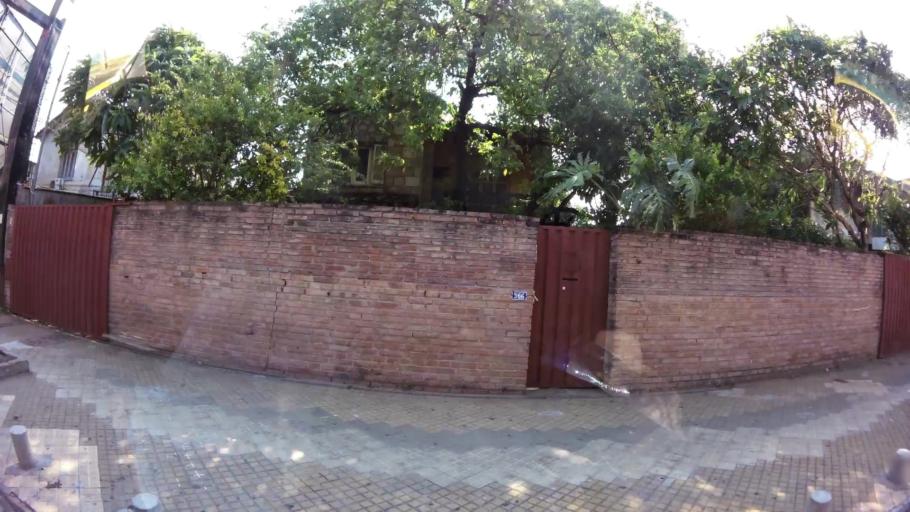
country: PY
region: Asuncion
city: Asuncion
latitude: -25.2991
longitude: -57.6321
